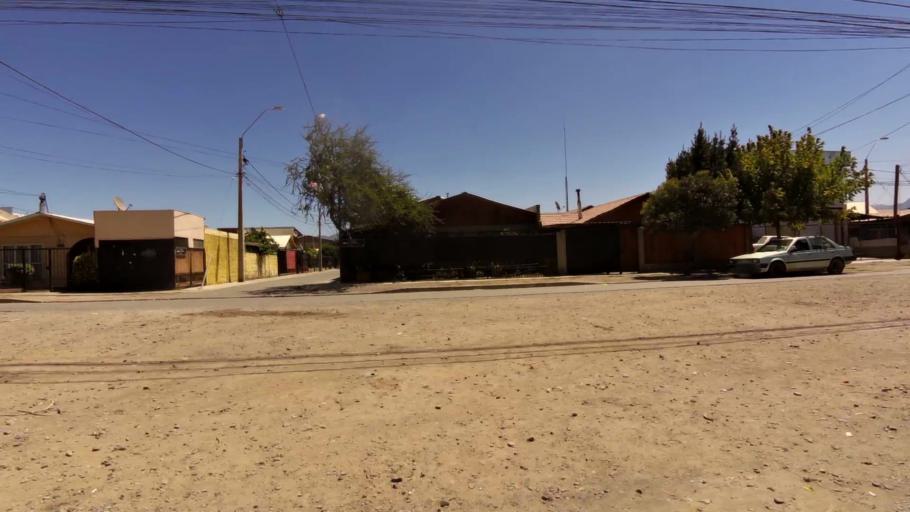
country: CL
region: O'Higgins
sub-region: Provincia de Cachapoal
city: Rancagua
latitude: -34.1645
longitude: -70.7584
